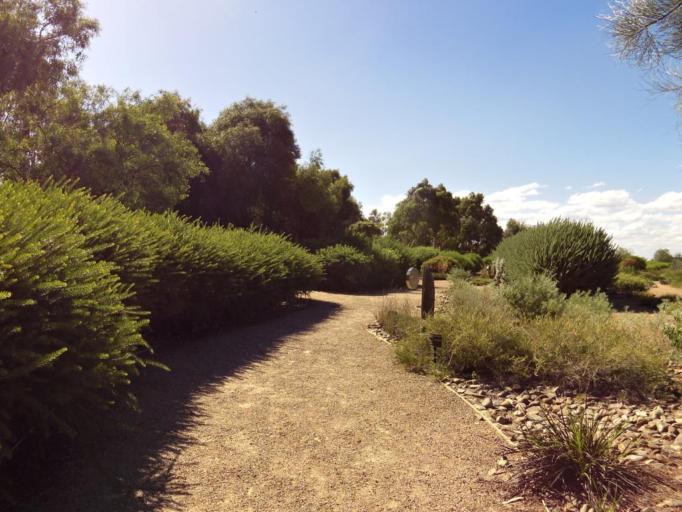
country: AU
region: Victoria
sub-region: Casey
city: Botanic Ridge
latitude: -38.1296
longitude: 145.2689
